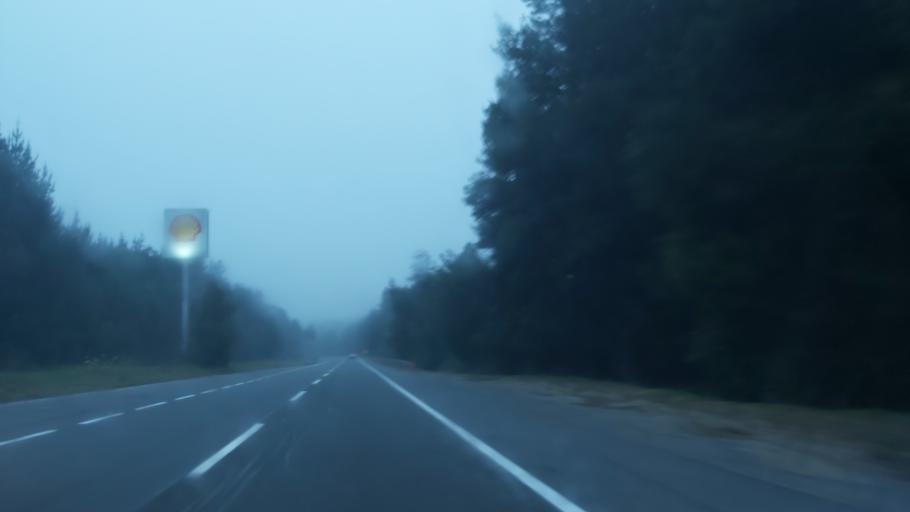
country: CL
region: Biobio
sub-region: Provincia de Concepcion
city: Penco
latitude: -36.7482
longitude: -72.9211
